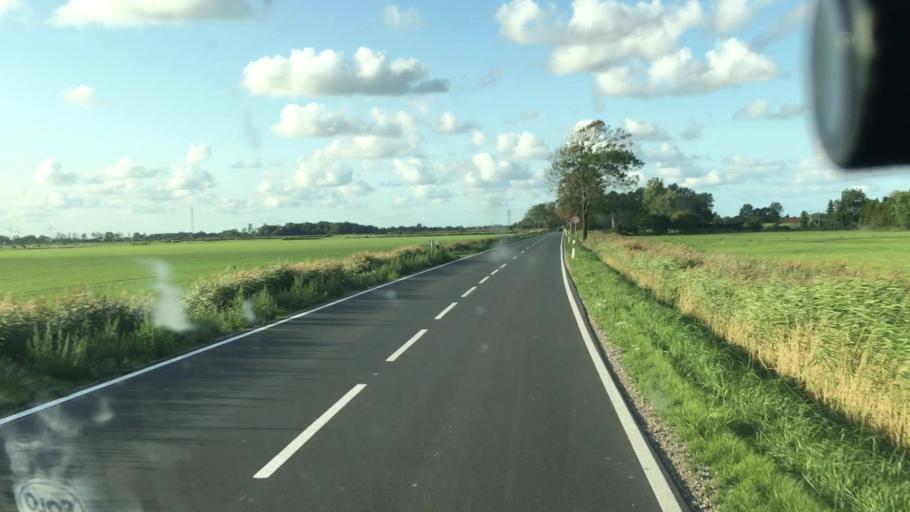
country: DE
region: Lower Saxony
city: Jever
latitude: 53.6273
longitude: 7.8617
